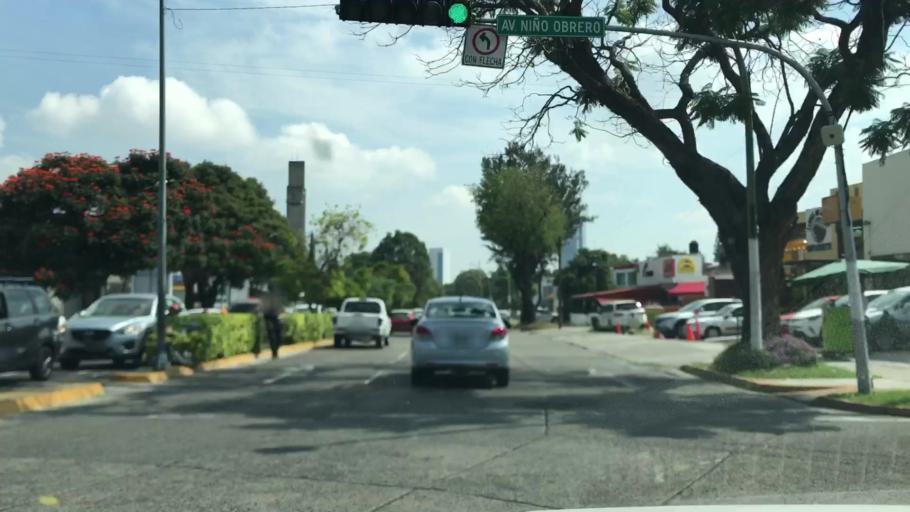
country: MX
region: Jalisco
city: Guadalajara
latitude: 20.6651
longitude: -103.4086
